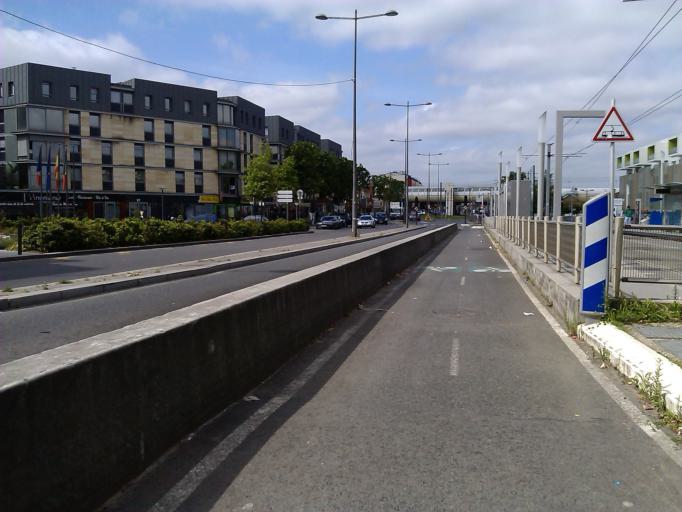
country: FR
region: Aquitaine
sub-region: Departement de la Gironde
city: Cenon
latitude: 44.8580
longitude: -0.5310
